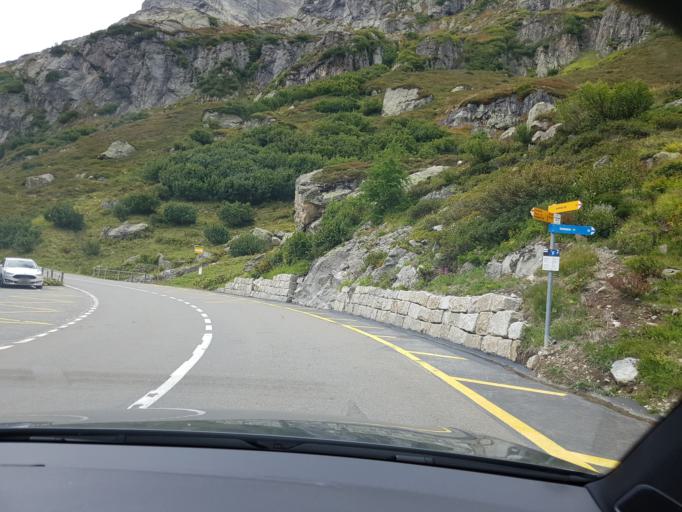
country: CH
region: Obwalden
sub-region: Obwalden
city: Engelberg
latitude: 46.7476
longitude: 8.4653
